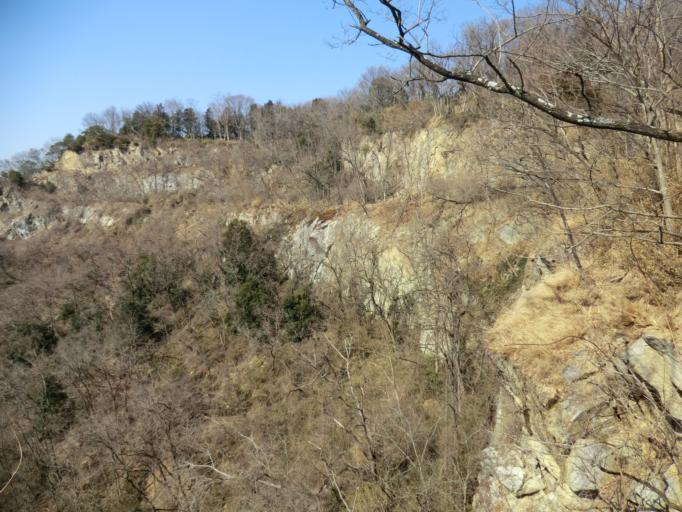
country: JP
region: Ibaraki
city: Tsukuba
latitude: 36.1556
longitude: 140.1173
